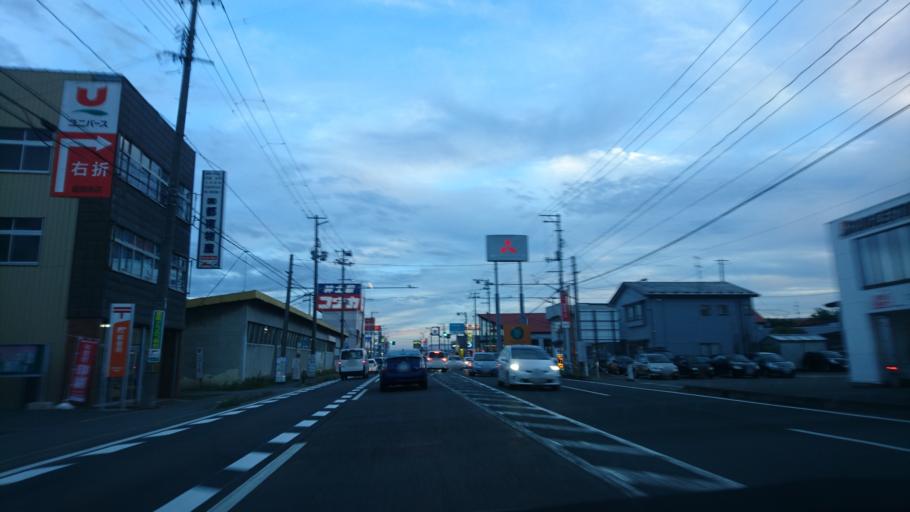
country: JP
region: Iwate
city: Morioka-shi
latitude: 39.6683
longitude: 141.1574
